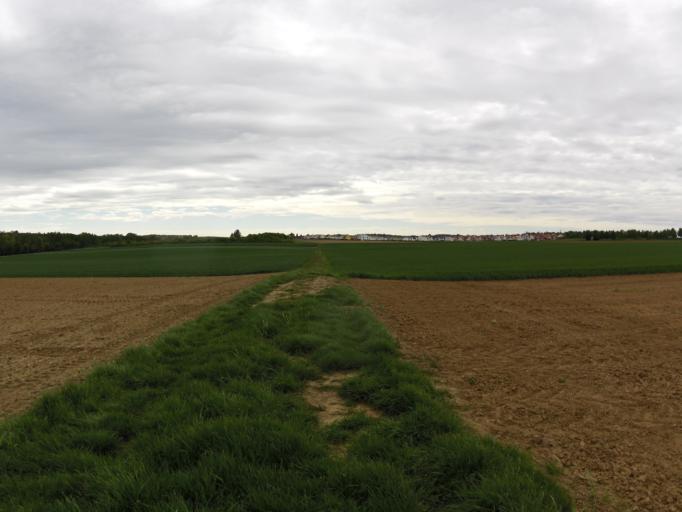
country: DE
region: Bavaria
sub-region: Regierungsbezirk Unterfranken
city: Unterpleichfeld
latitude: 49.8501
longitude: 10.0626
